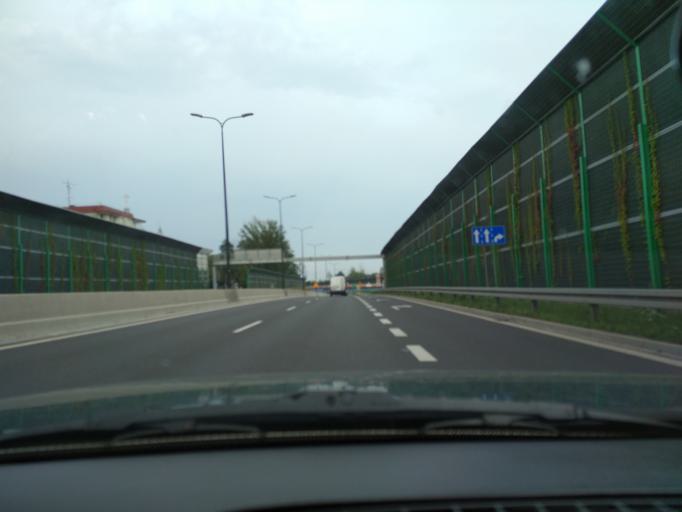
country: PL
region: Silesian Voivodeship
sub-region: Gliwice
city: Gliwice
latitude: 50.2933
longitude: 18.6862
